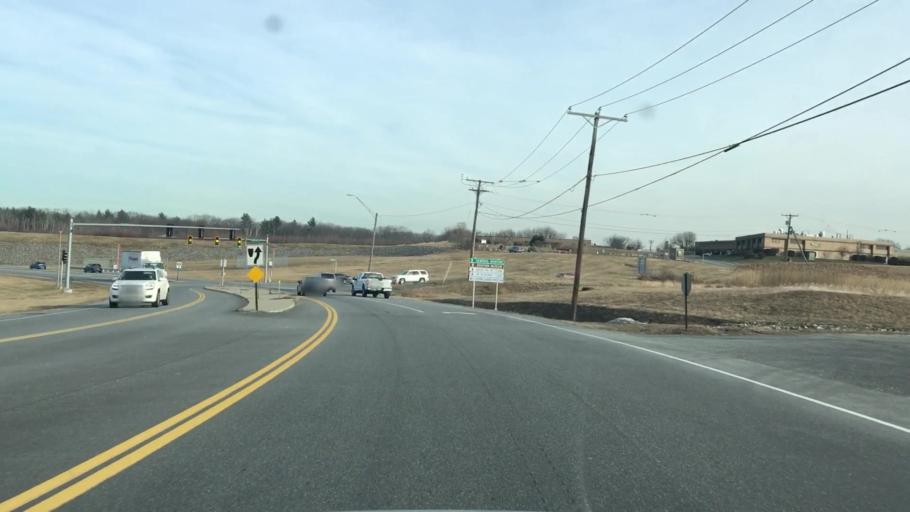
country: US
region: New Hampshire
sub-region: Rockingham County
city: Londonderry
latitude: 42.9143
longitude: -71.4258
